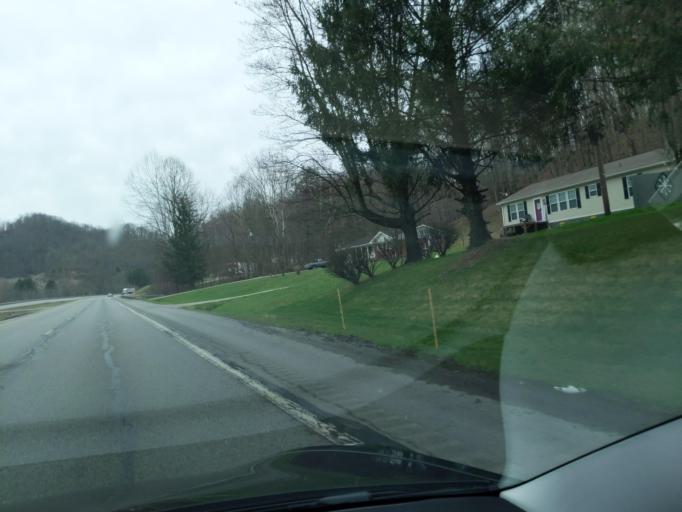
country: US
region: Kentucky
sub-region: Knox County
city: Barbourville
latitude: 36.8754
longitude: -83.8182
